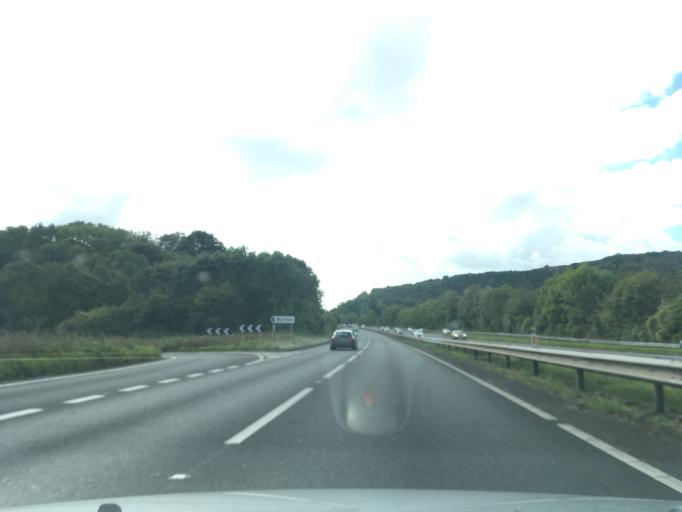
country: GB
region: England
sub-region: Hampshire
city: Petersfield
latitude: 50.9839
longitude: -0.9637
